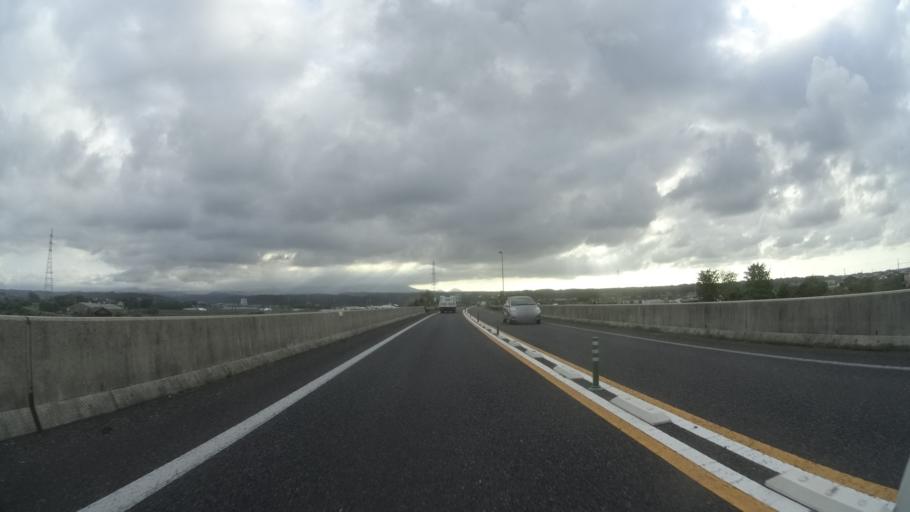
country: JP
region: Tottori
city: Kurayoshi
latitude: 35.4866
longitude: 133.7028
